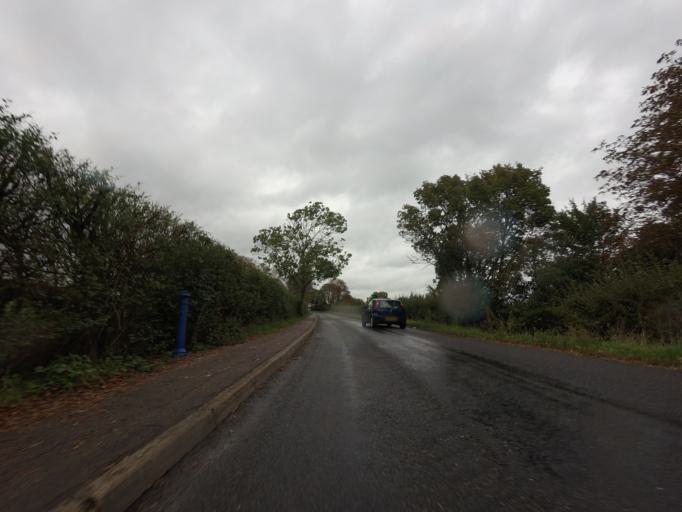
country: GB
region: England
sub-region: Cambridgeshire
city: Comberton
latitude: 52.1607
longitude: -0.0015
